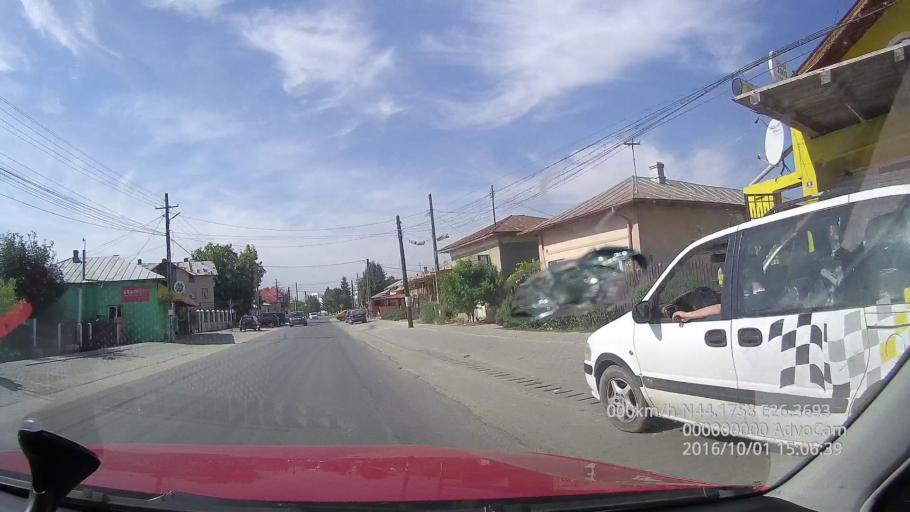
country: RO
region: Giurgiu
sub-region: Comuna Hotarele
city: Hotarele
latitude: 44.1773
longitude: 26.3674
